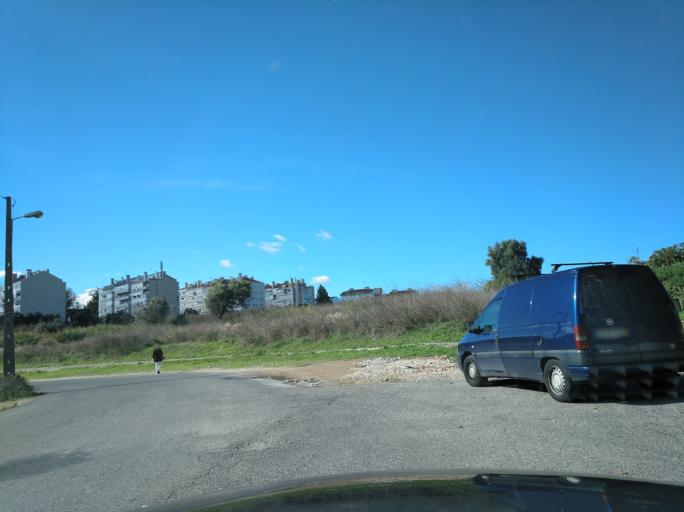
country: PT
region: Lisbon
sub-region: Lisbon
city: Lisbon
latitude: 38.7356
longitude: -9.1103
